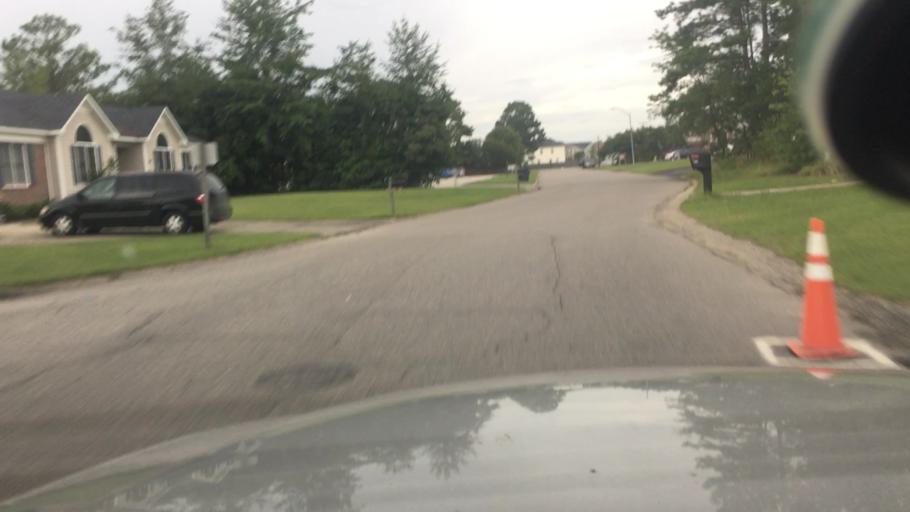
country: US
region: North Carolina
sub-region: Cumberland County
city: Hope Mills
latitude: 34.9739
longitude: -78.9764
